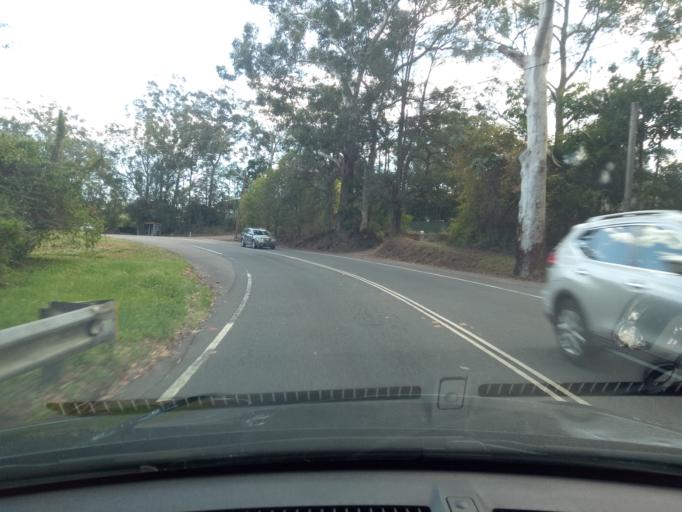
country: AU
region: New South Wales
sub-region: Gosford Shire
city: Narara
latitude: -33.3895
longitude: 151.3549
